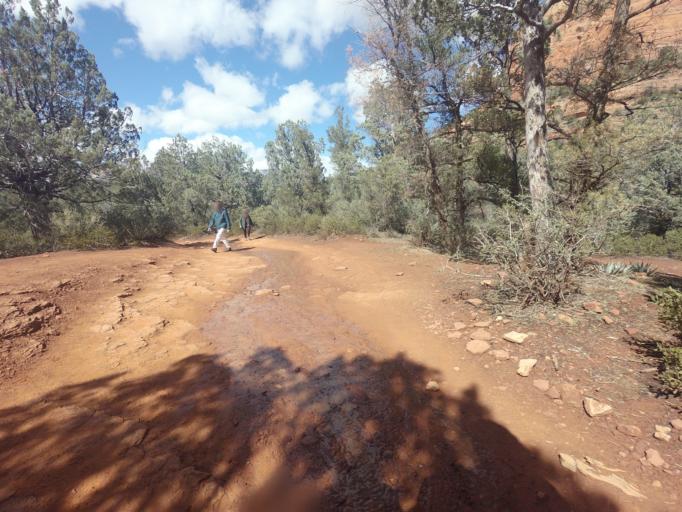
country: US
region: Arizona
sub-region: Yavapai County
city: West Sedona
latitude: 34.9018
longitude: -111.8093
